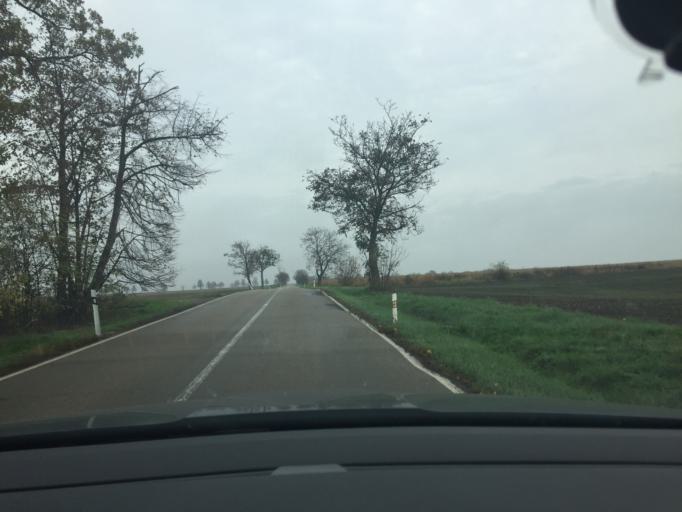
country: CZ
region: South Moravian
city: Blazovice
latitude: 49.1432
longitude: 16.7819
